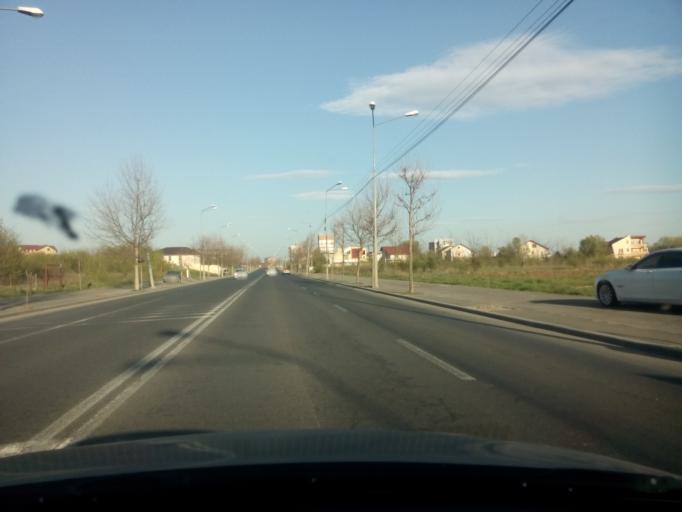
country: RO
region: Ilfov
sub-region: Comuna Mogosoaia
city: Mogosoaia
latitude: 44.5060
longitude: 26.0303
